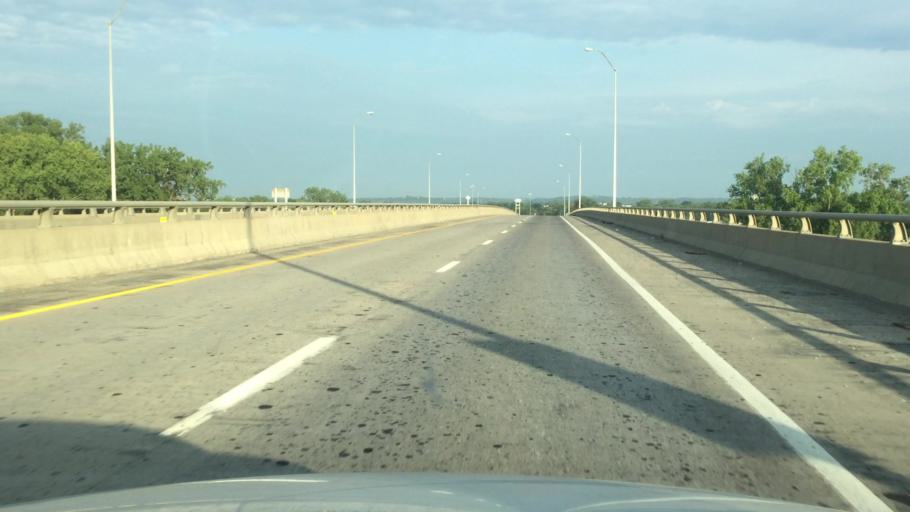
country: US
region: Kansas
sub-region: Doniphan County
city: Elwood
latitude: 39.7490
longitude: -94.8602
